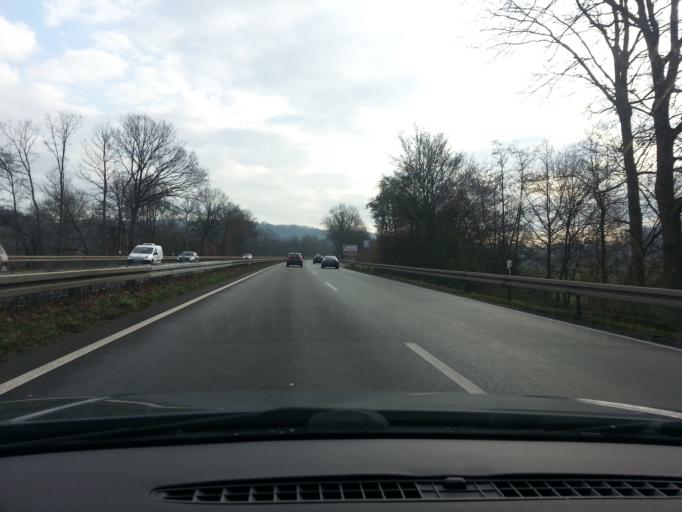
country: DE
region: Saarland
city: Homburg
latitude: 49.2939
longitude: 7.3063
